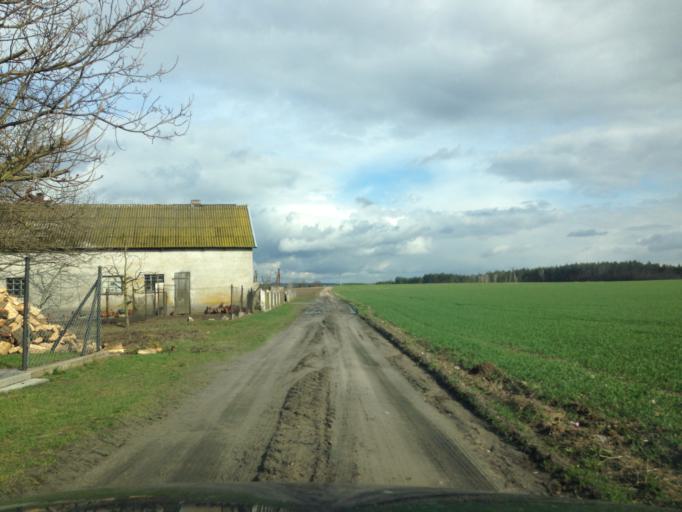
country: PL
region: Kujawsko-Pomorskie
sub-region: Powiat brodnicki
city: Bartniczka
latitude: 53.2492
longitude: 19.5783
